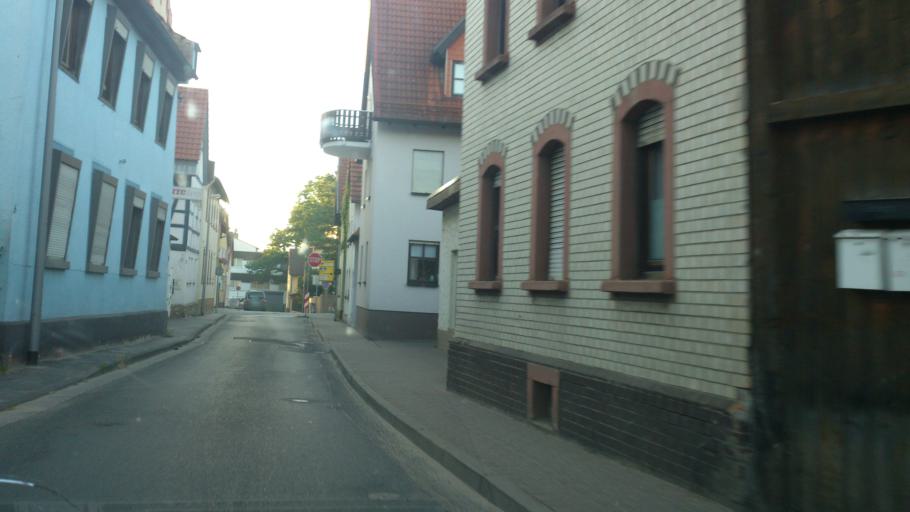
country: DE
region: Hesse
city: Kelsterbach
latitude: 50.0525
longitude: 8.5000
